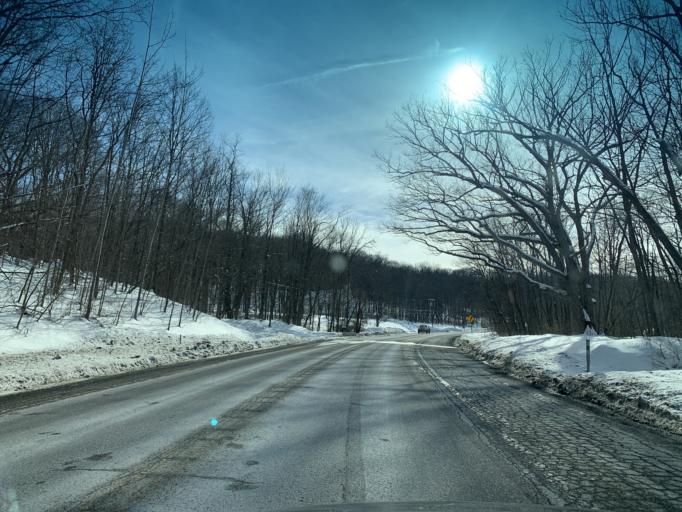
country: US
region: Maryland
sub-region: Allegany County
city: Frostburg
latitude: 39.6216
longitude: -78.9003
